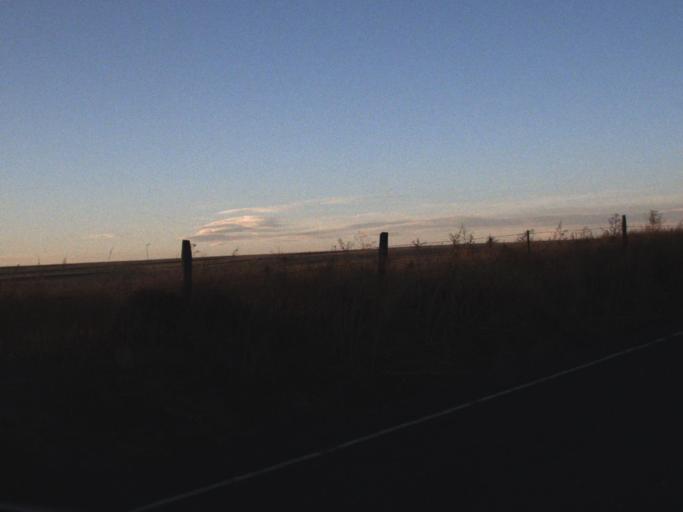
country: US
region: Washington
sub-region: Adams County
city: Ritzville
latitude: 47.0674
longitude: -118.6630
